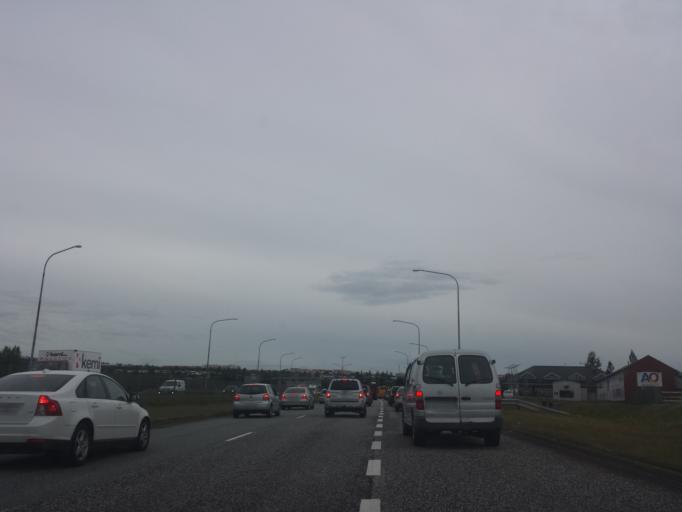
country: IS
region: Capital Region
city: Reykjavik
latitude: 64.1221
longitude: -21.8478
